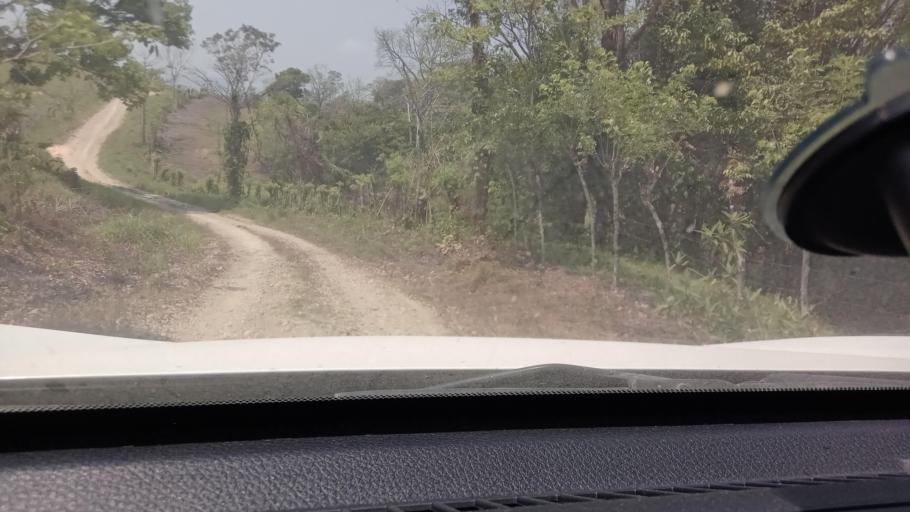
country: MX
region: Tabasco
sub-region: Huimanguillo
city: Francisco Rueda
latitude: 17.4869
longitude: -93.9340
